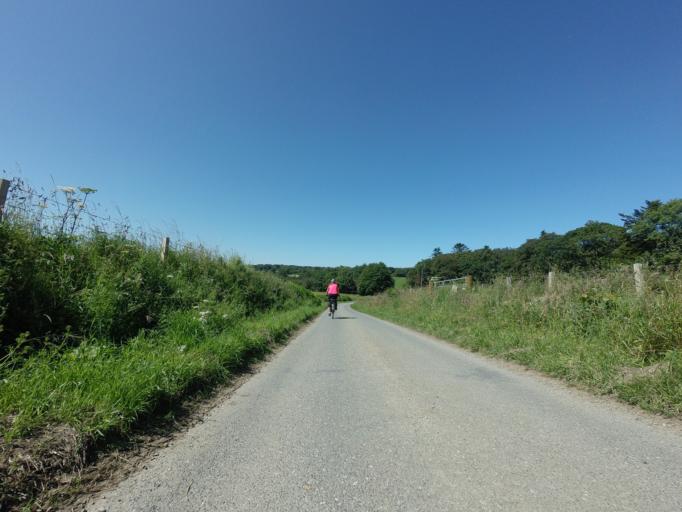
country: GB
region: Scotland
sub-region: Aberdeenshire
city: Macduff
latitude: 57.6421
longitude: -2.5046
